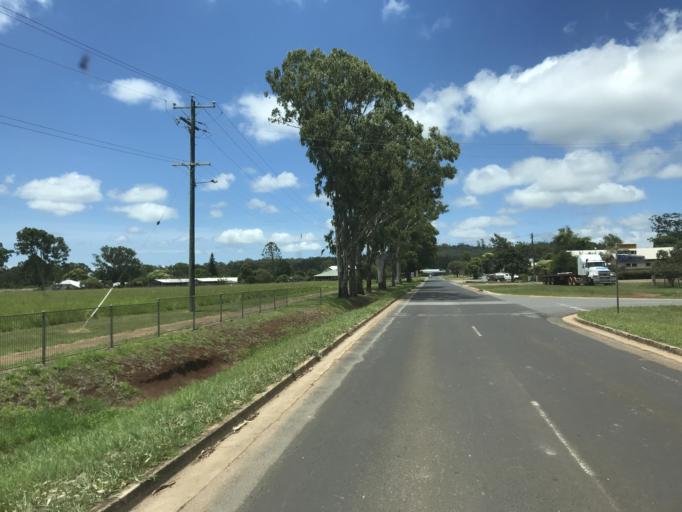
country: AU
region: Queensland
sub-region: Tablelands
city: Ravenshoe
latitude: -17.6142
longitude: 145.4868
